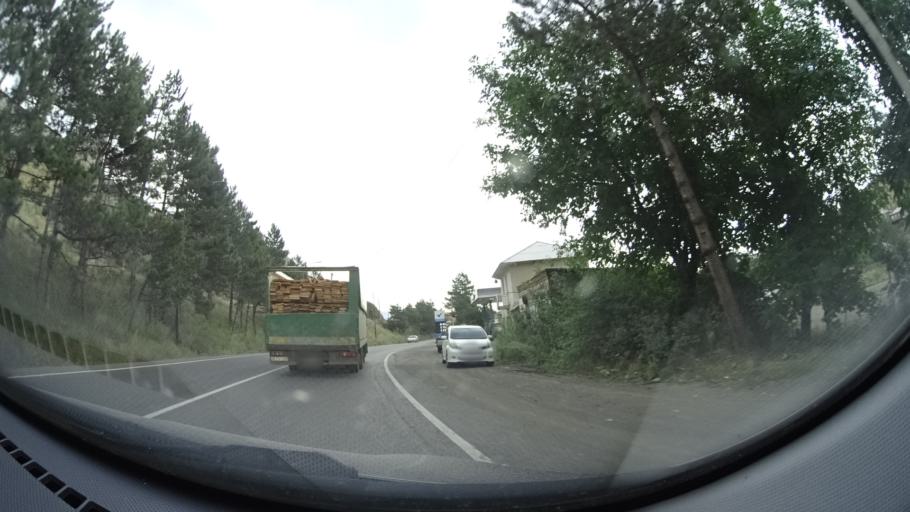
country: GE
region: Samtskhe-Javakheti
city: Akhaltsikhe
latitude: 41.6412
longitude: 42.9768
